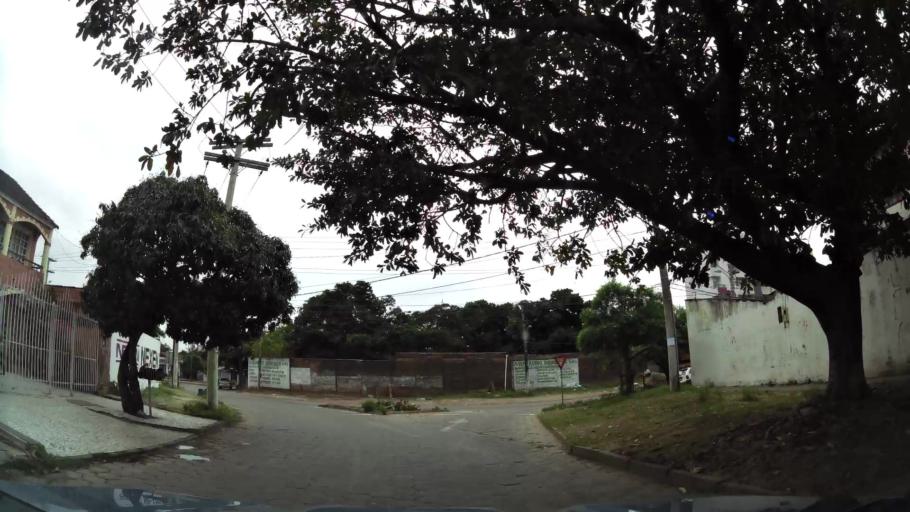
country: BO
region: Santa Cruz
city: Santa Cruz de la Sierra
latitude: -17.7586
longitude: -63.1820
